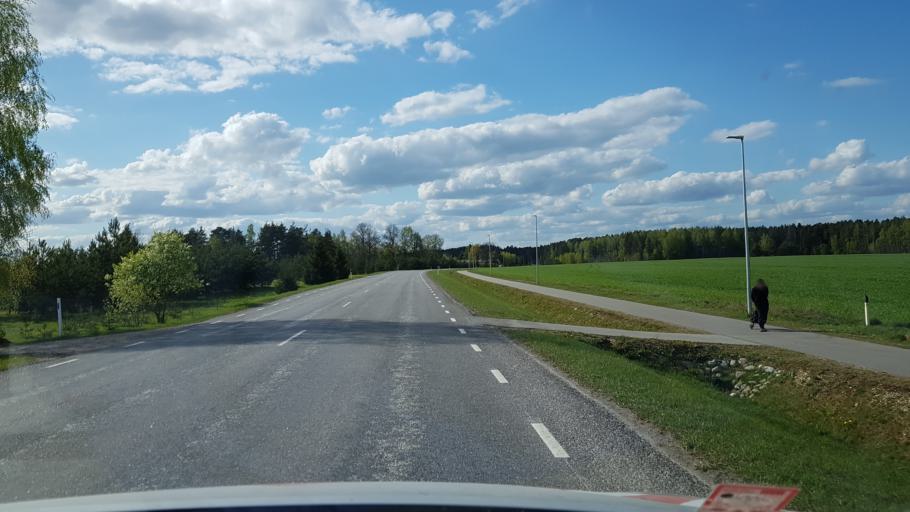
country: EE
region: Tartu
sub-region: UElenurme vald
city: Ulenurme
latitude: 58.3085
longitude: 26.8509
